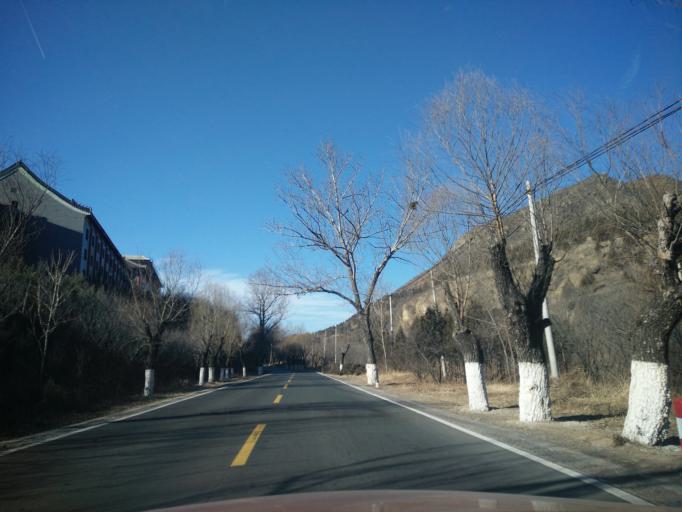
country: CN
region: Beijing
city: Yanchi
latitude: 40.0016
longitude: 115.7788
